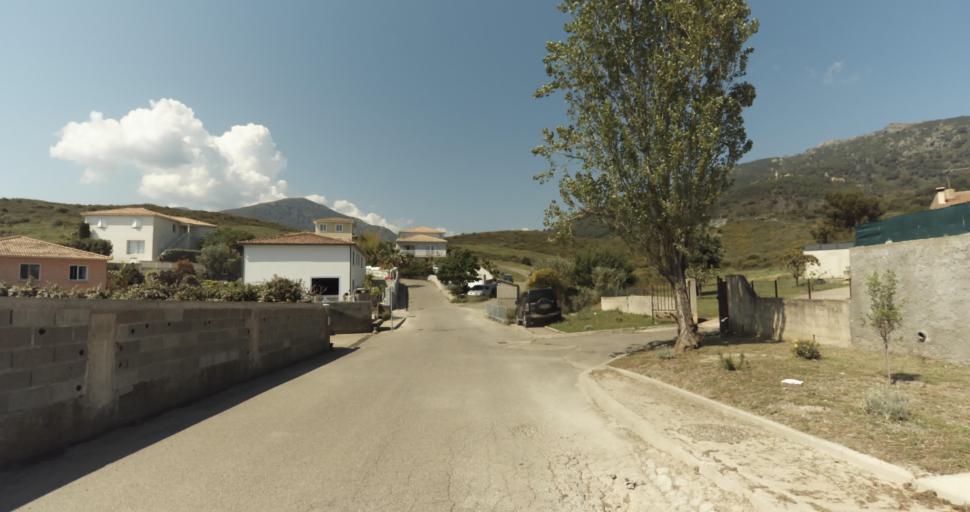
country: FR
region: Corsica
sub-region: Departement de la Haute-Corse
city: Biguglia
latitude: 42.6144
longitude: 9.4282
